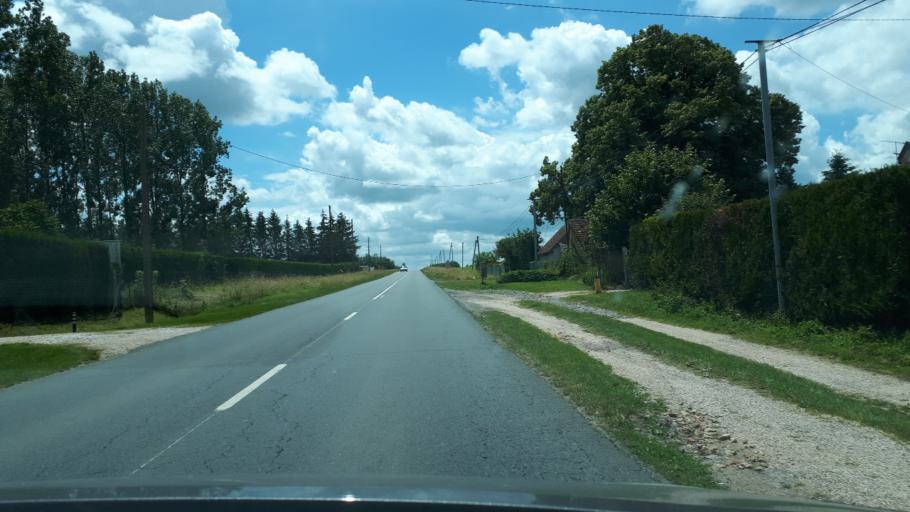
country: FR
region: Centre
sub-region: Departement du Loir-et-Cher
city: Contres
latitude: 47.4047
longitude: 1.4177
